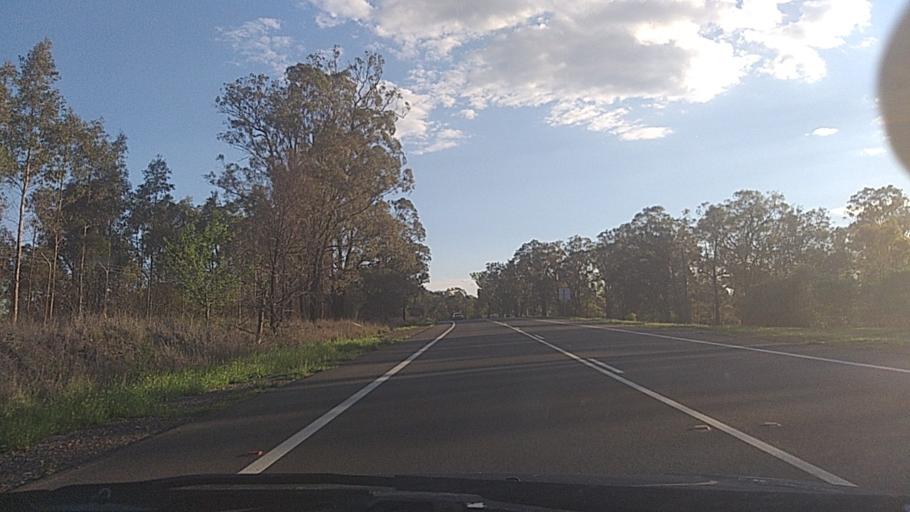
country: AU
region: New South Wales
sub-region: Camden
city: Camden South
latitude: -34.1100
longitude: 150.6968
